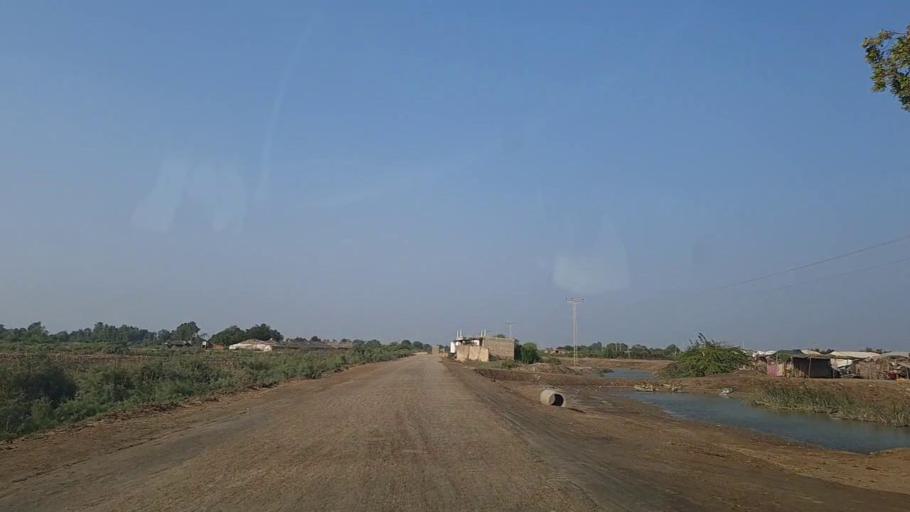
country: PK
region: Sindh
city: Mirpur Sakro
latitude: 24.5683
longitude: 67.6701
